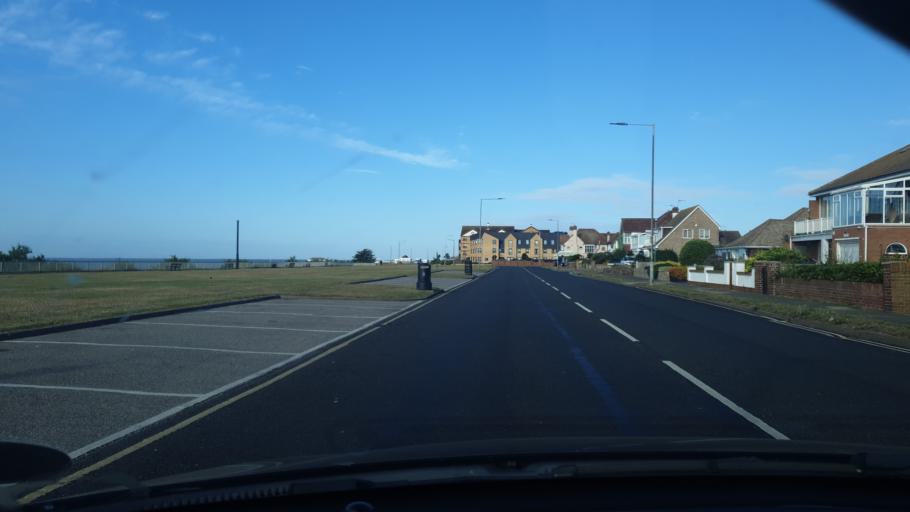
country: GB
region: England
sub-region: Essex
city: Clacton-on-Sea
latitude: 51.7956
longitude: 1.1757
